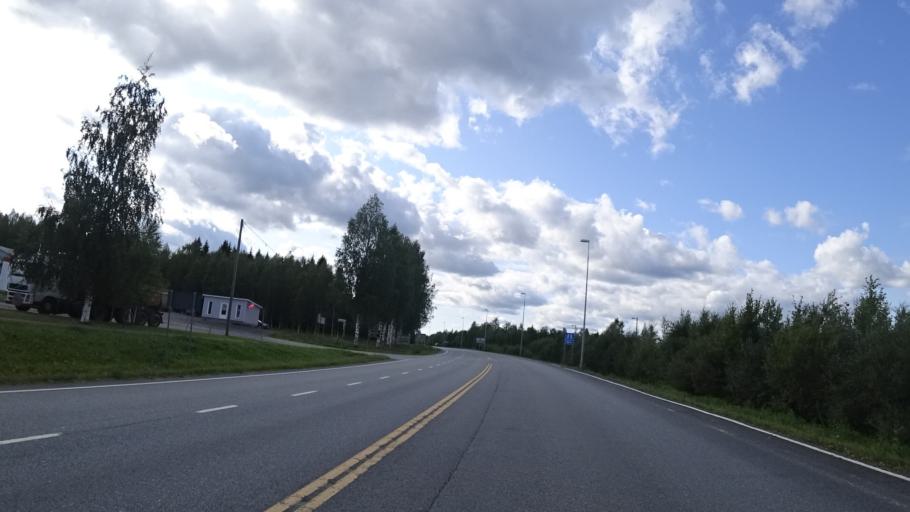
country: RU
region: Republic of Karelia
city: Vyartsilya
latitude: 62.1761
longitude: 30.5898
